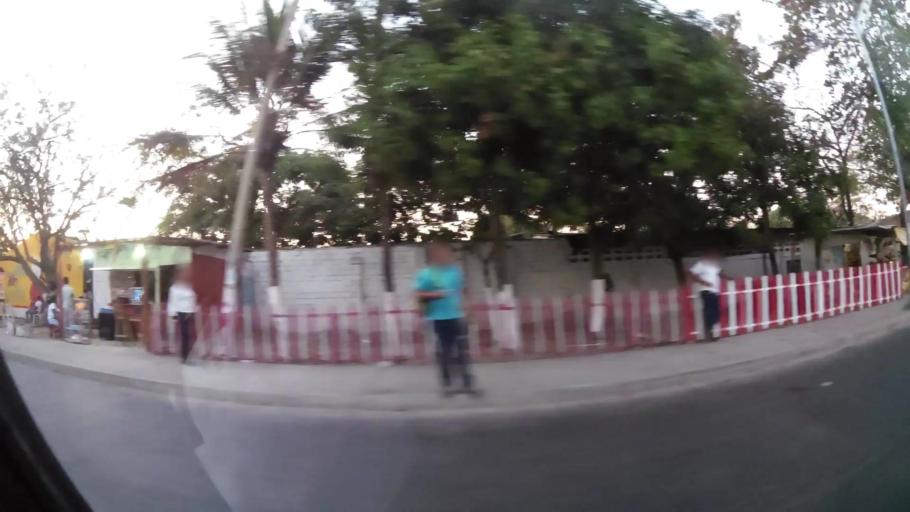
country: CO
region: Atlantico
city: Barranquilla
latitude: 10.9443
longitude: -74.7770
